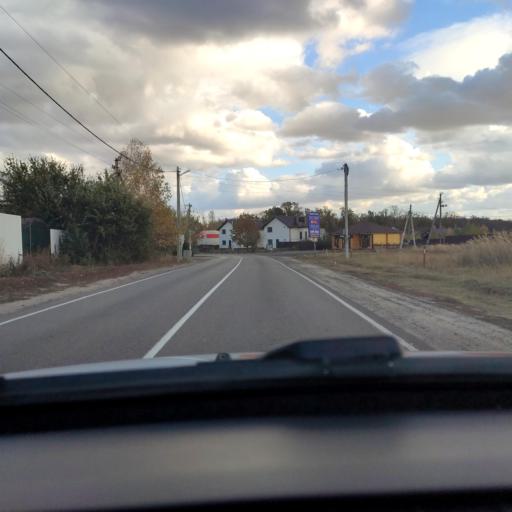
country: RU
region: Voronezj
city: Ramon'
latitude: 51.8260
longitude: 39.2566
